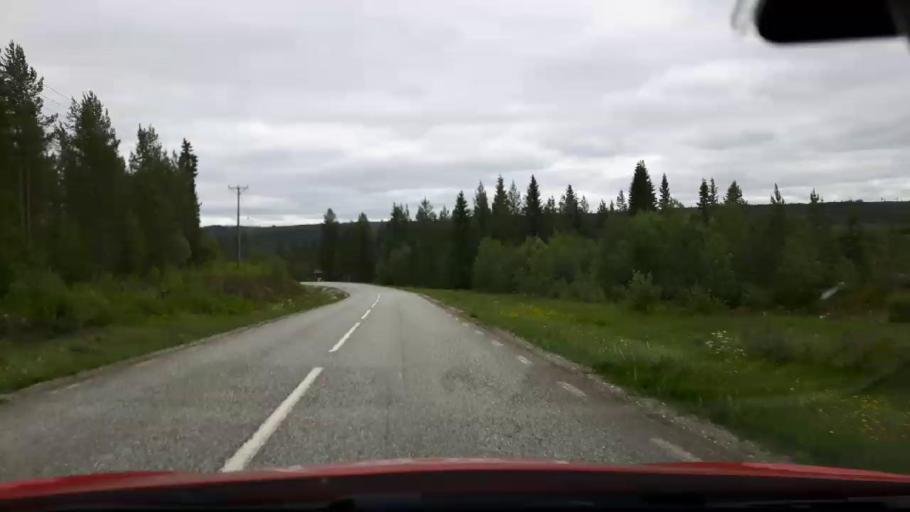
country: SE
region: Jaemtland
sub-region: Stroemsunds Kommun
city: Stroemsund
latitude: 63.2943
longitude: 15.7704
